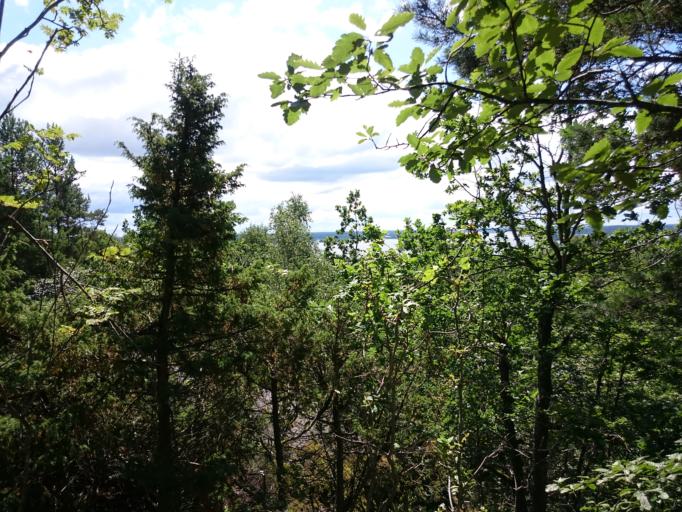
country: SE
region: OEstergoetland
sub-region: Norrkopings Kommun
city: Krokek
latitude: 58.6610
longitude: 16.4301
